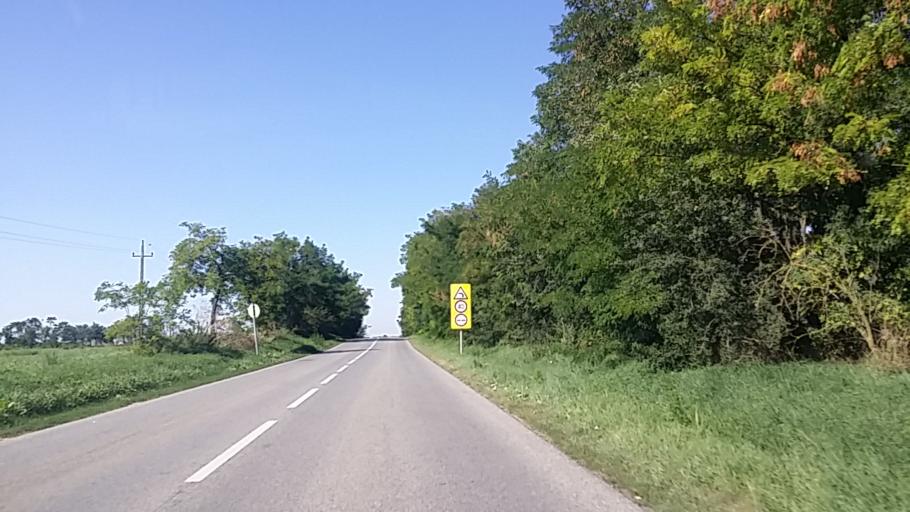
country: HU
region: Fejer
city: Mezofalva
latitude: 46.8994
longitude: 18.7119
